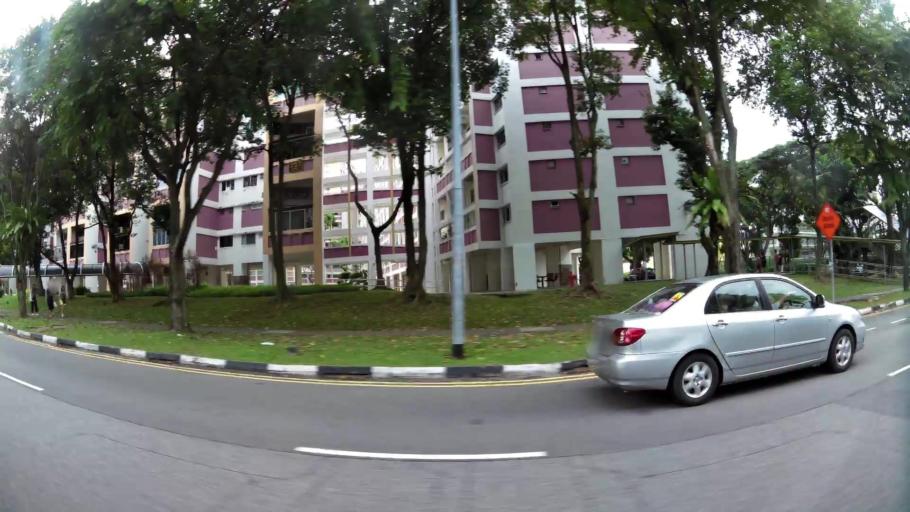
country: SG
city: Singapore
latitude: 1.3404
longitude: 103.8531
